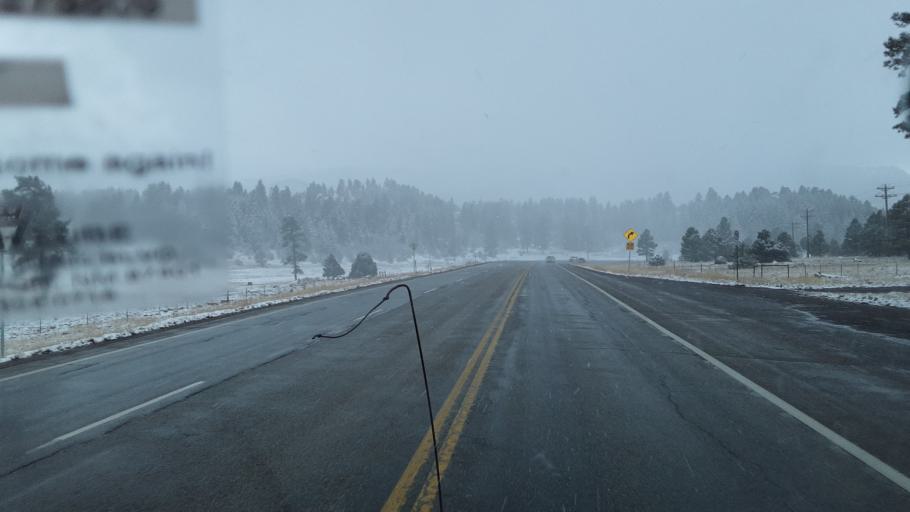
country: US
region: Colorado
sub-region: Archuleta County
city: Pagosa Springs
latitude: 37.2315
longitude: -107.1067
